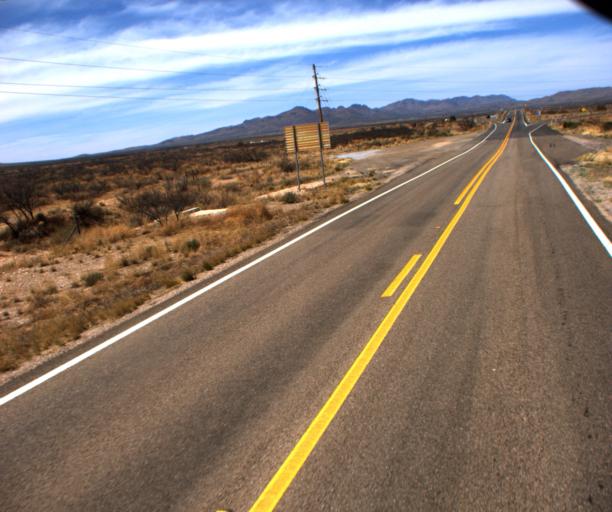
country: US
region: Arizona
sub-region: Cochise County
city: Willcox
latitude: 32.1718
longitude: -109.9471
